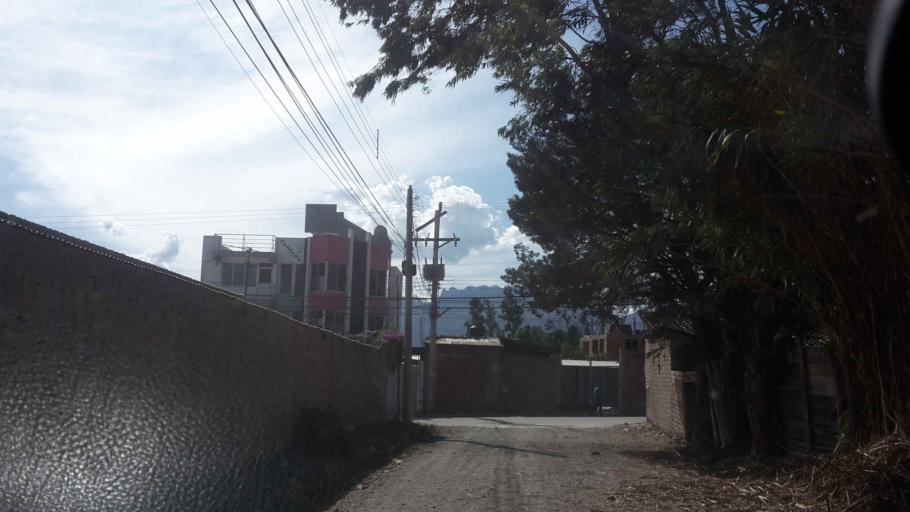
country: BO
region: Cochabamba
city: Cochabamba
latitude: -17.3488
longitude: -66.2049
